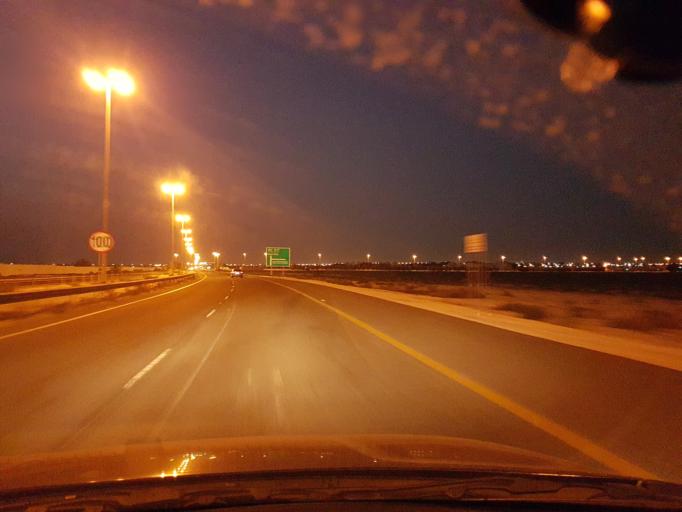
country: BH
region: Central Governorate
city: Dar Kulayb
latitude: 26.0332
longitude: 50.4999
